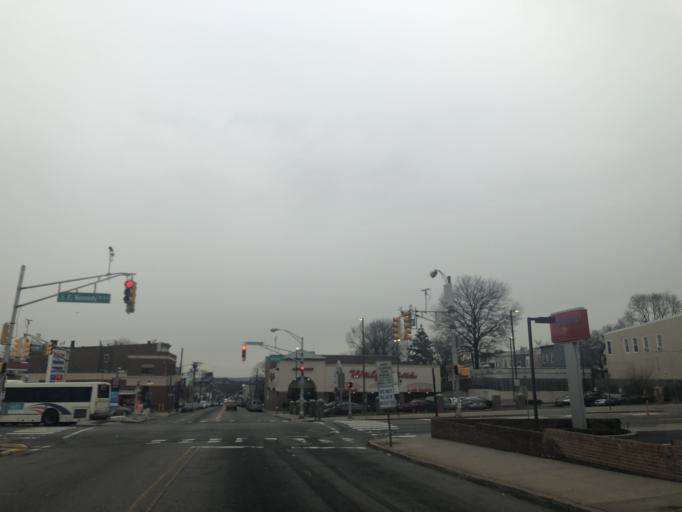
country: US
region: New Jersey
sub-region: Hudson County
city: Jersey City
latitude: 40.7192
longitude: -74.0773
